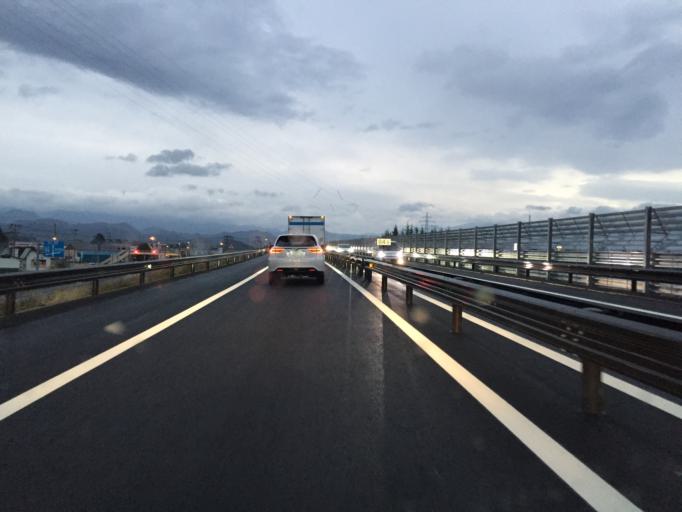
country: JP
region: Yamagata
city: Yonezawa
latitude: 37.9442
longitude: 140.1187
